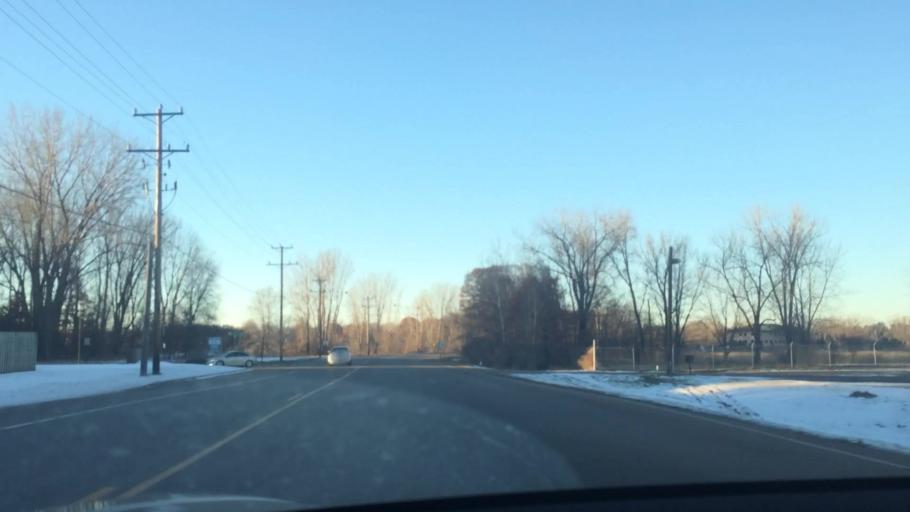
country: US
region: Minnesota
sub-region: Anoka County
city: Circle Pines
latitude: 45.1484
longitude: -93.1332
